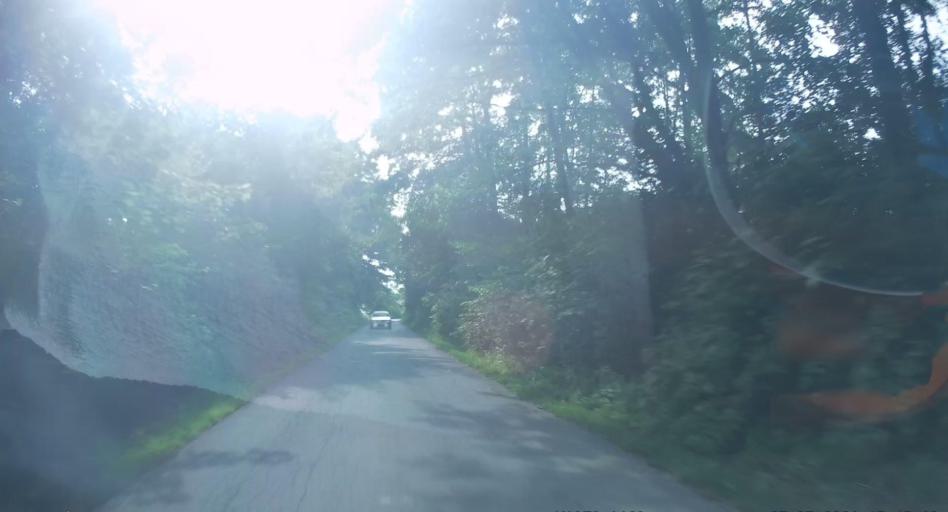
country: PL
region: Lodz Voivodeship
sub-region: Powiat rawski
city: Rawa Mazowiecka
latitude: 51.7011
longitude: 20.2450
